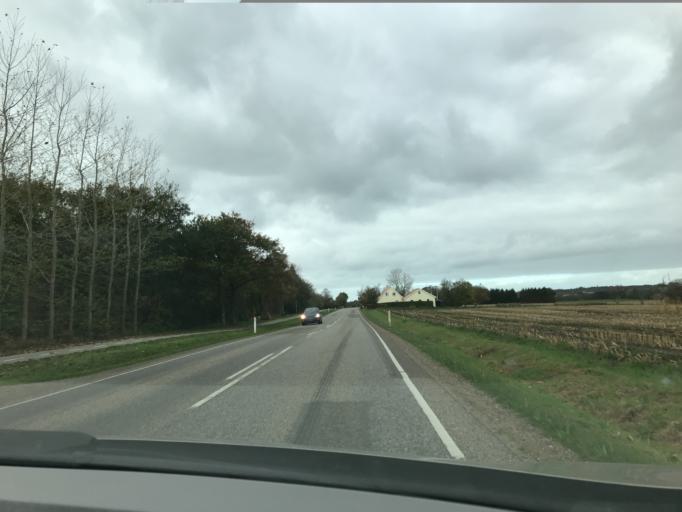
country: DK
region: South Denmark
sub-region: Varde Kommune
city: Olgod
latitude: 55.7973
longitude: 8.6473
